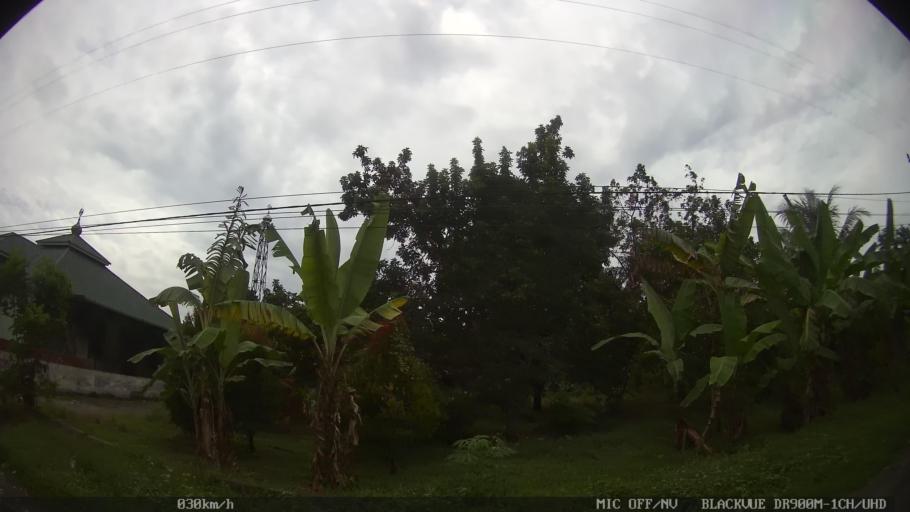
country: ID
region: North Sumatra
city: Sunggal
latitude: 3.5785
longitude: 98.5648
